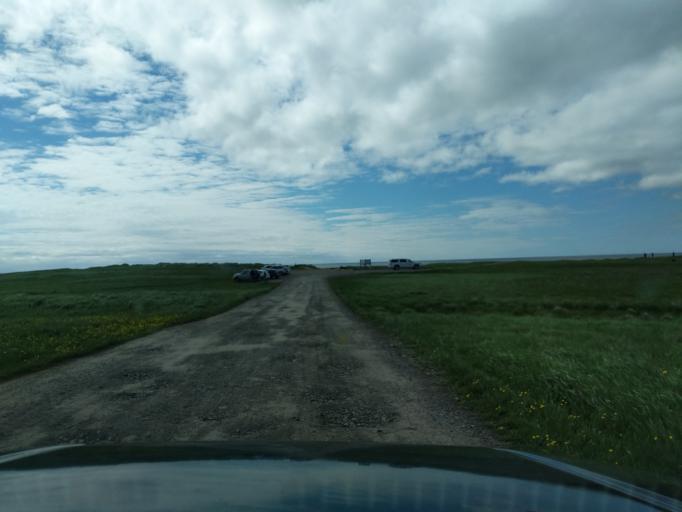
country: IS
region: West
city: Stykkisholmur
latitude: 64.8045
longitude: -23.0802
